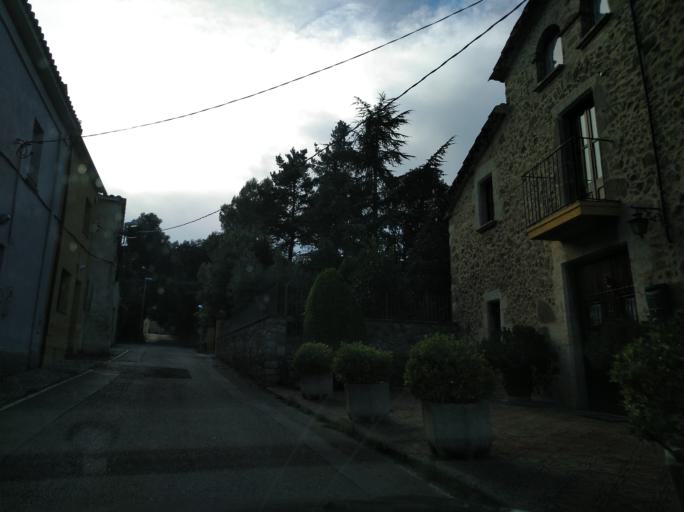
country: ES
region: Catalonia
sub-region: Provincia de Girona
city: Aiguaviva
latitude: 41.9416
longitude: 2.7746
